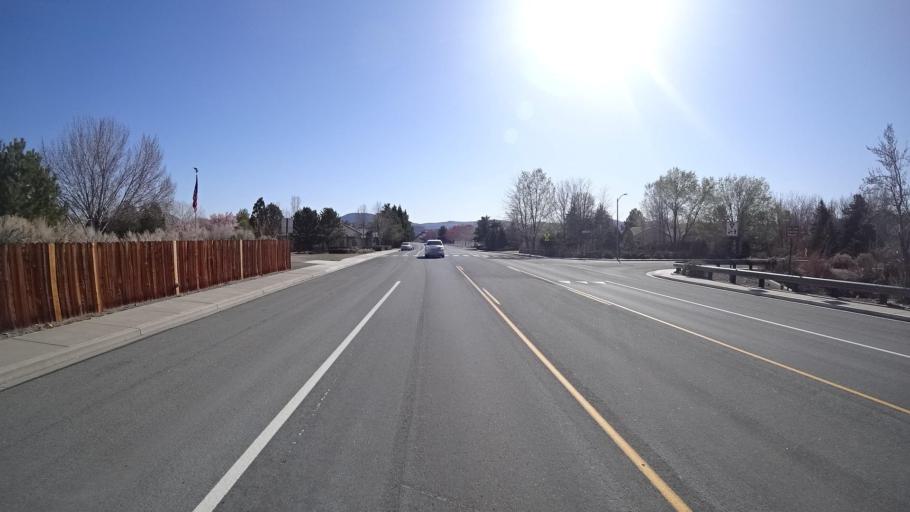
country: US
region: Nevada
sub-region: Washoe County
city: Reno
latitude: 39.4550
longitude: -119.7859
